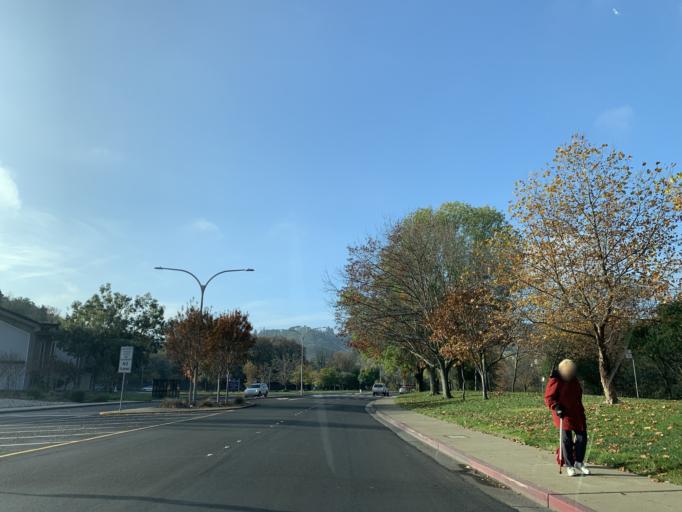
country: US
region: California
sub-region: Contra Costa County
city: Saranap
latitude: 37.8760
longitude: -122.0721
